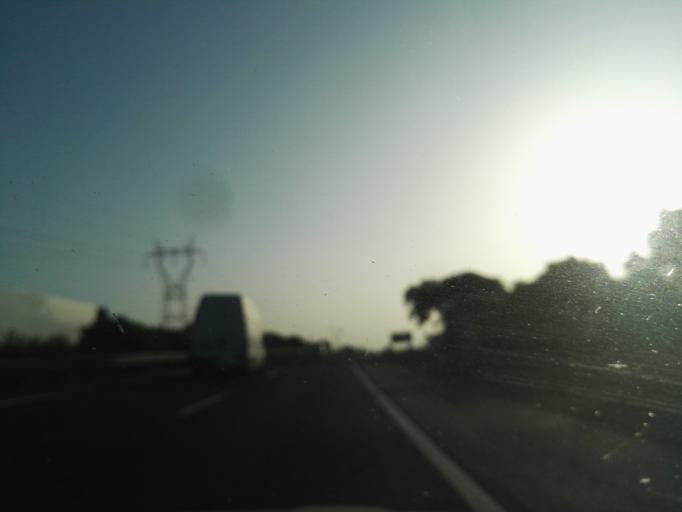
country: PT
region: Setubal
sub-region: Moita
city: Moita
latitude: 38.6516
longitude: -8.9680
